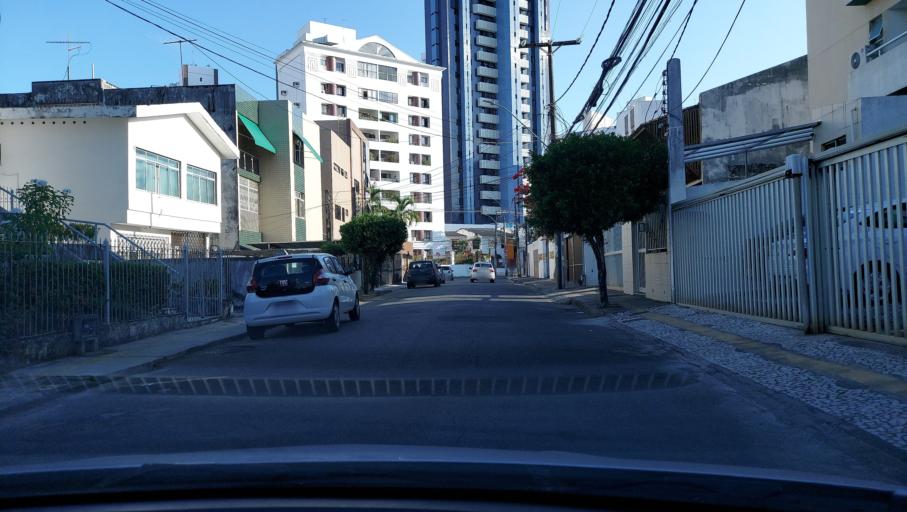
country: BR
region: Bahia
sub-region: Salvador
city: Salvador
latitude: -12.9958
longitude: -38.4540
